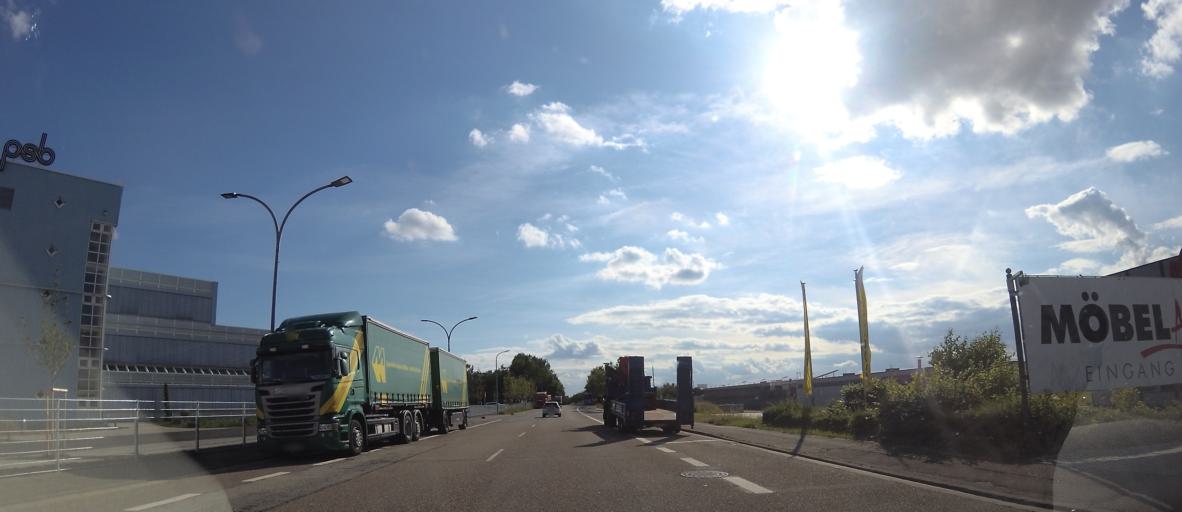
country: DE
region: Rheinland-Pfalz
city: Pirmasens
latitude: 49.1871
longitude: 7.5895
